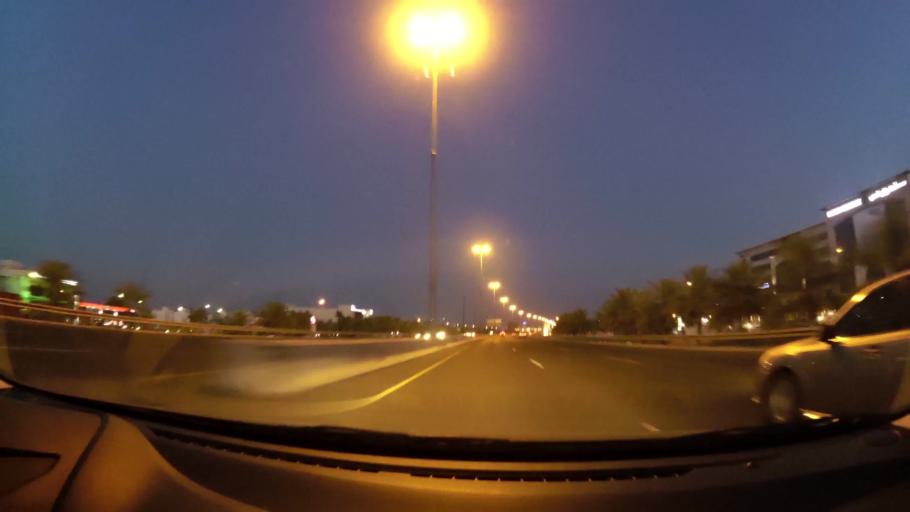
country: OM
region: Muhafazat Masqat
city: As Sib al Jadidah
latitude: 23.6486
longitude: 58.2170
